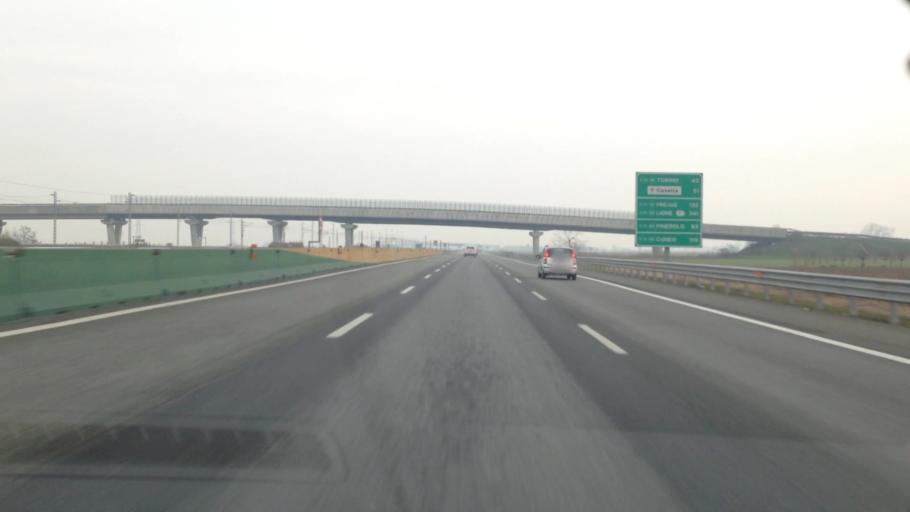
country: IT
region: Piedmont
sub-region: Provincia di Vercelli
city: Alice Castello
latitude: 45.3563
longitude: 8.1105
